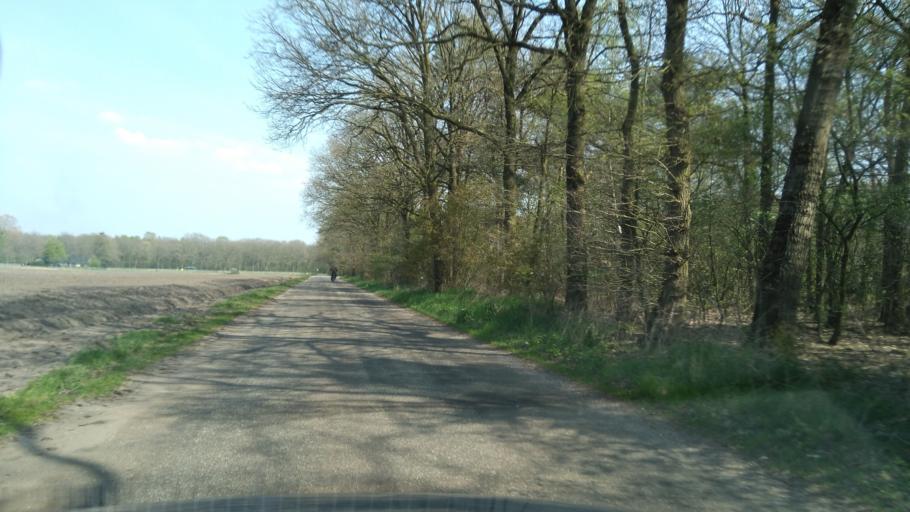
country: BE
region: Flanders
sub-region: Provincie Antwerpen
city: Baarle-Hertog
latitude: 51.4050
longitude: 4.9260
